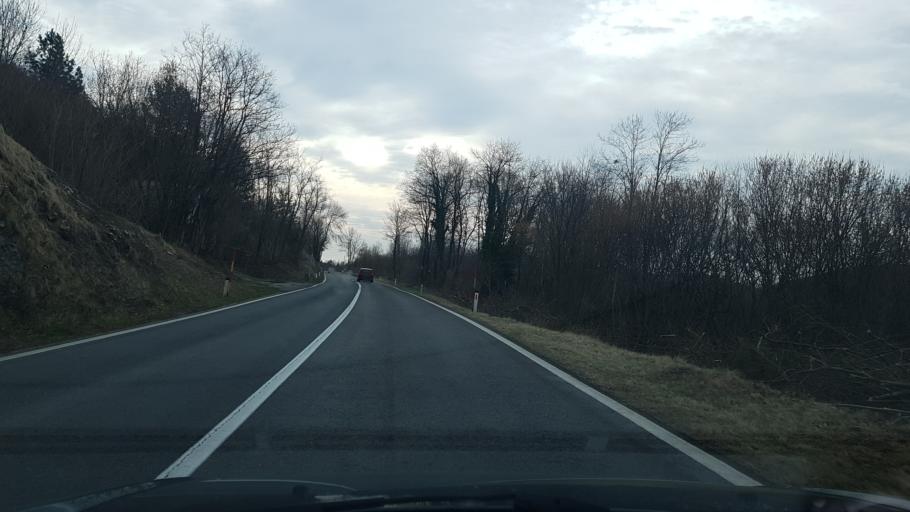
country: SI
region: Ilirska Bistrica
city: Ilirska Bistrica
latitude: 45.4987
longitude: 14.1860
